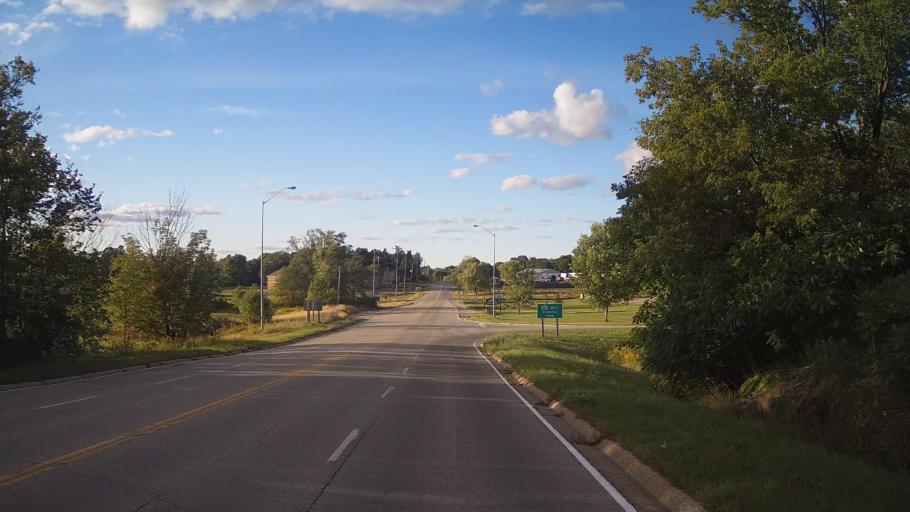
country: CA
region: Ontario
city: Gananoque
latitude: 44.3458
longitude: -76.1712
